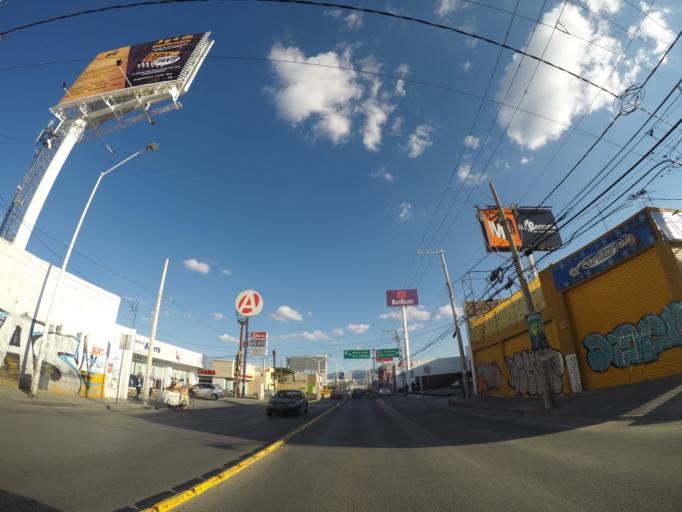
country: MX
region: San Luis Potosi
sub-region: San Luis Potosi
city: San Luis Potosi
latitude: 22.1673
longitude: -101.0015
